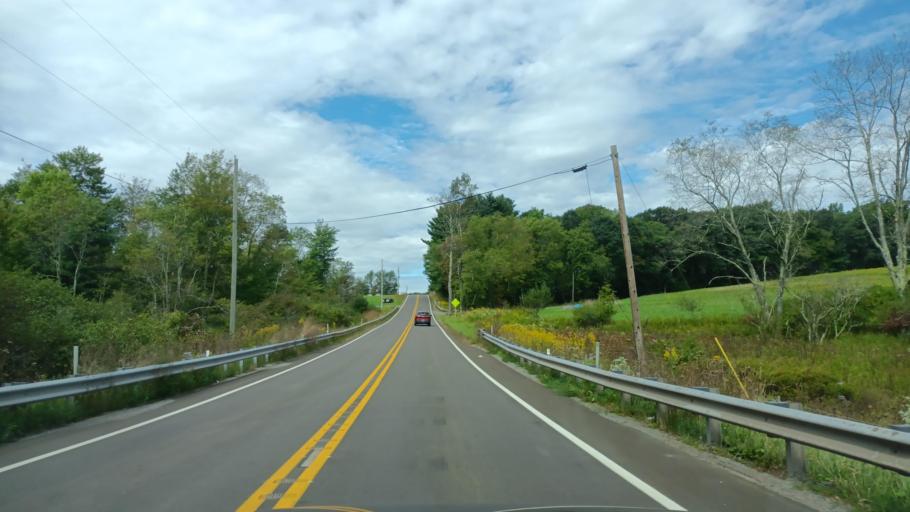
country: US
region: Maryland
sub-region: Garrett County
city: Oakland
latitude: 39.3104
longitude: -79.4748
